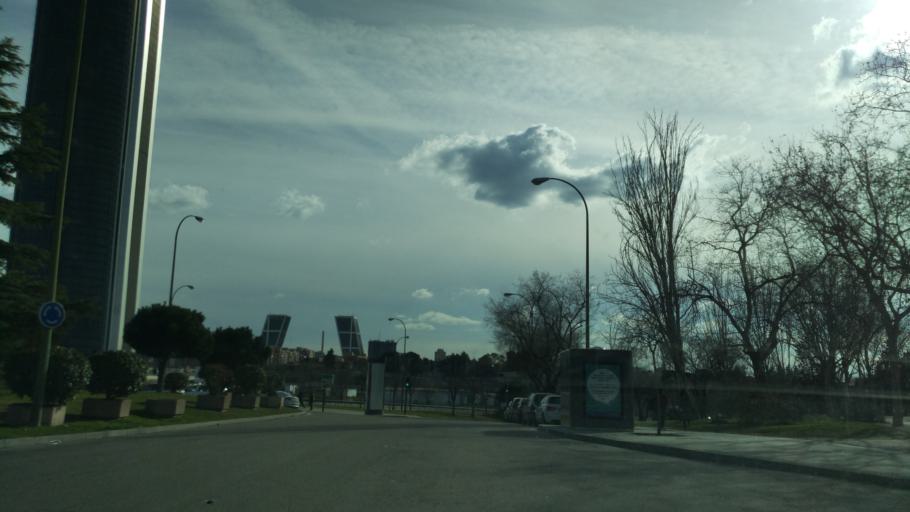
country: ES
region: Madrid
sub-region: Provincia de Madrid
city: Pinar de Chamartin
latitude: 40.4806
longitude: -3.6895
